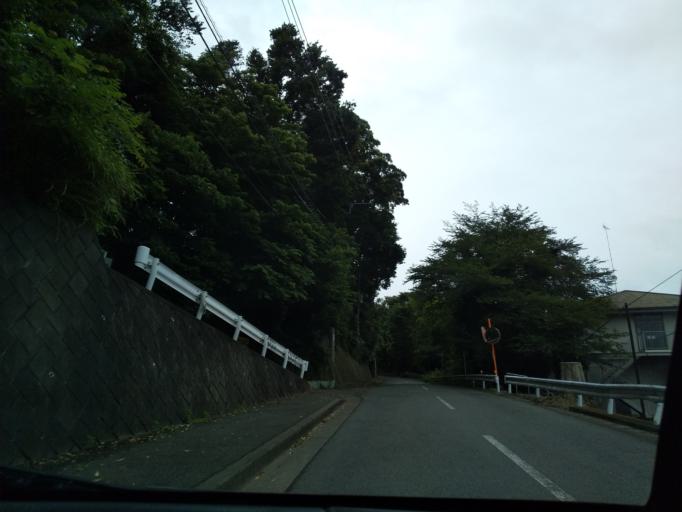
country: JP
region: Kanagawa
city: Minami-rinkan
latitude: 35.4282
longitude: 139.4433
